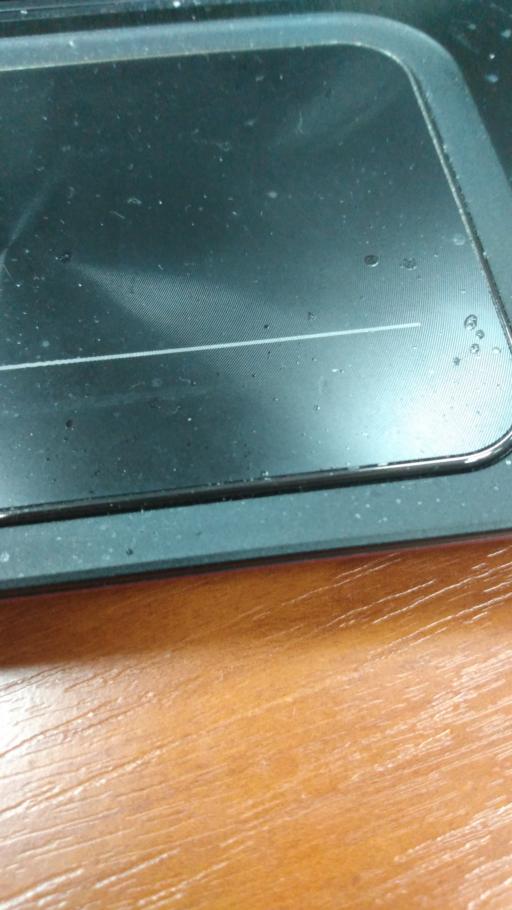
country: SR
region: Saramacca
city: Groningen
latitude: 5.7505
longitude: -55.4002
